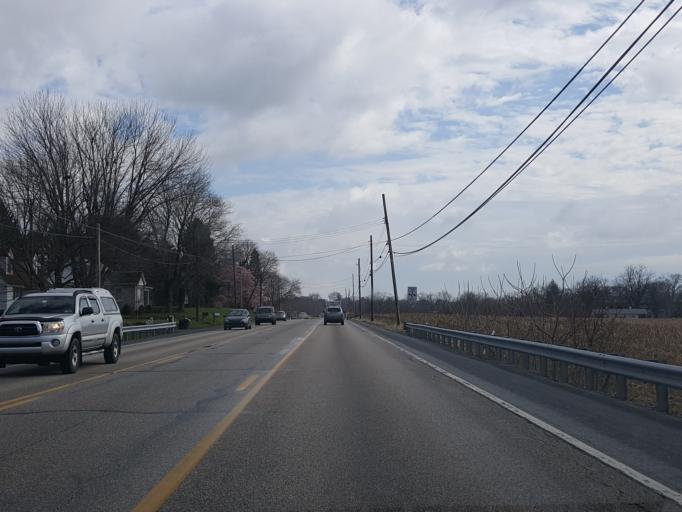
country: US
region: Pennsylvania
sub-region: Lebanon County
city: Myerstown
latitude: 40.3656
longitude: -76.3444
